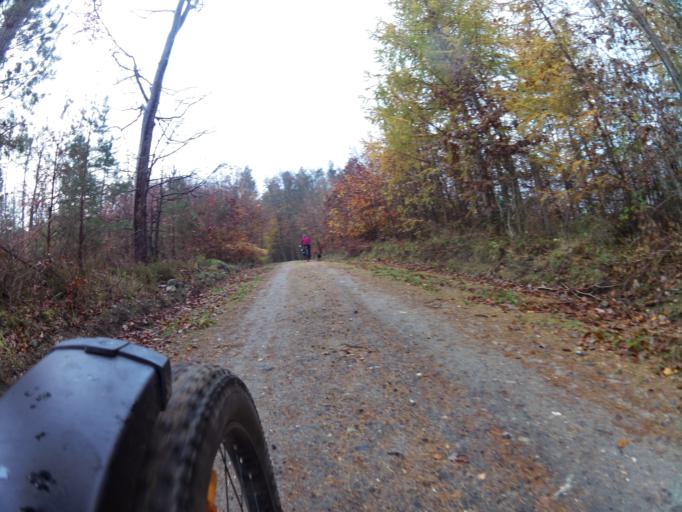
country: PL
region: Pomeranian Voivodeship
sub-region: Powiat pucki
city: Krokowa
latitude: 54.7755
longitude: 18.0913
